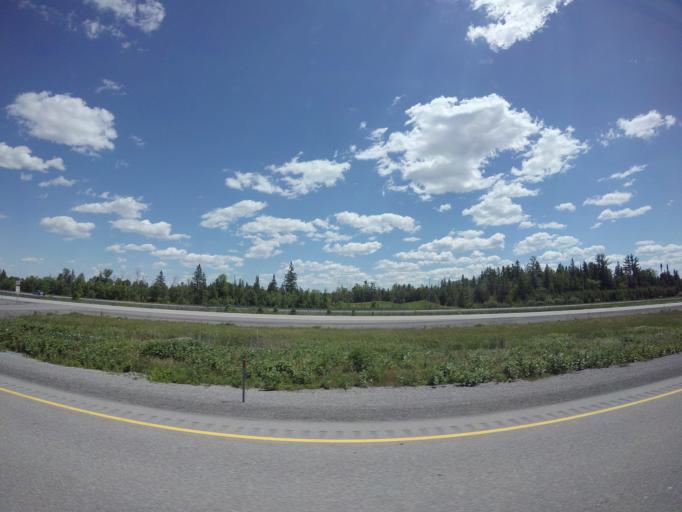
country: CA
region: Ontario
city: Carleton Place
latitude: 45.2179
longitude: -76.0169
